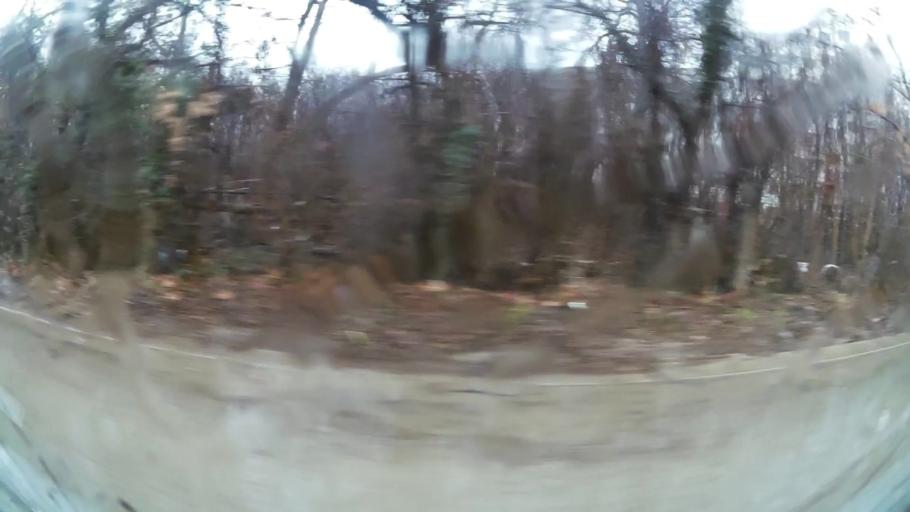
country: BG
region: Sofia-Capital
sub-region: Stolichna Obshtina
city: Sofia
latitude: 42.6294
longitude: 23.3656
